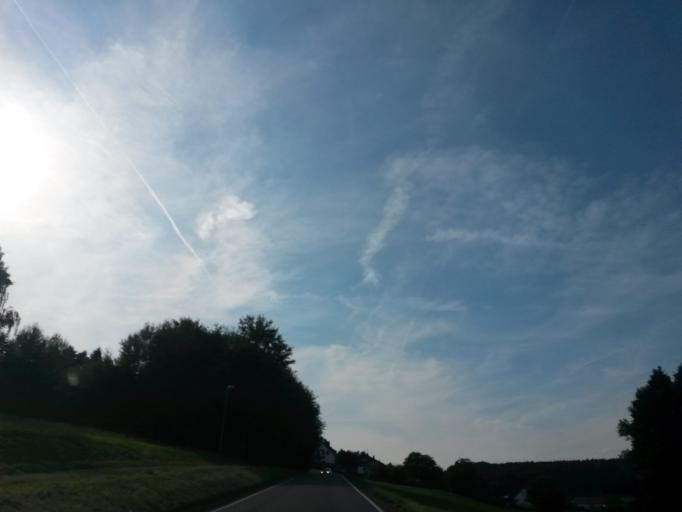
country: DE
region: North Rhine-Westphalia
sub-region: Regierungsbezirk Koln
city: Overath
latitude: 50.9657
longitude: 7.3139
